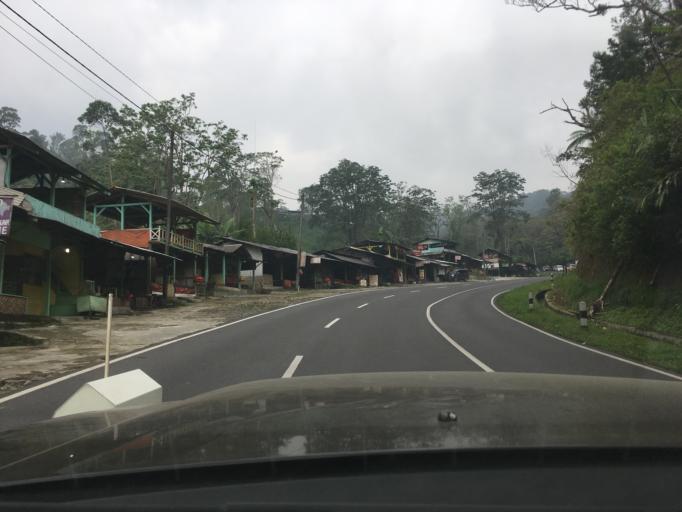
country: ID
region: West Java
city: Lembang
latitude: -6.7682
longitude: 107.6393
